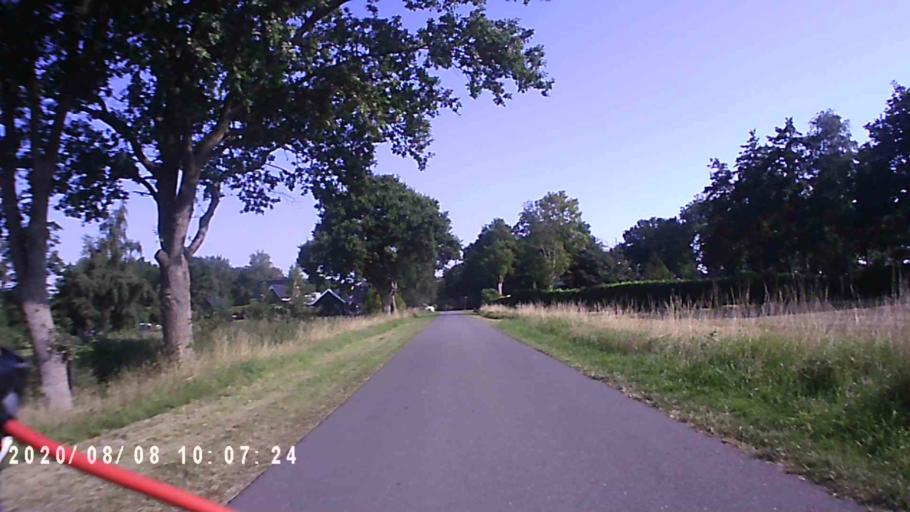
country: NL
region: Groningen
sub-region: Gemeente Leek
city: Leek
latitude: 53.1205
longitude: 6.3656
